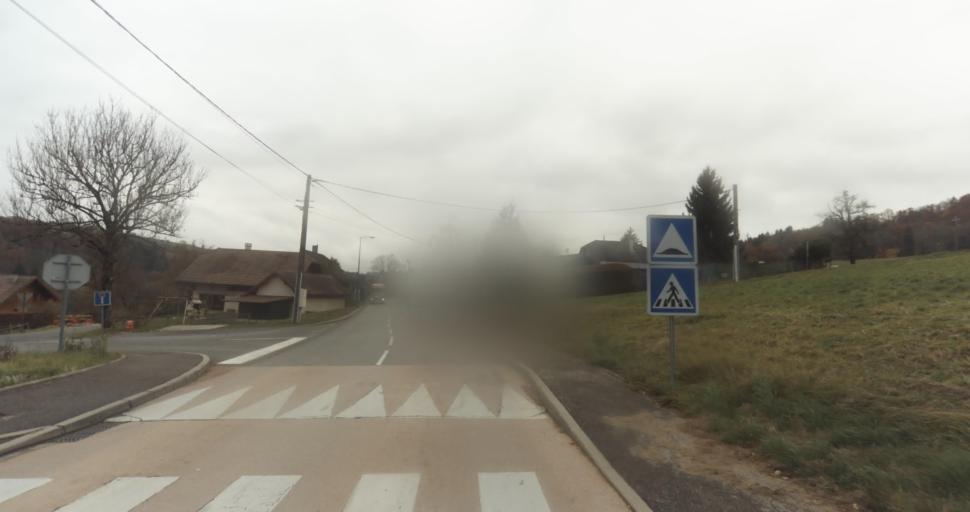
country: FR
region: Rhone-Alpes
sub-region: Departement de la Haute-Savoie
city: Thorens-Glieres
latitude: 45.9986
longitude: 6.2205
